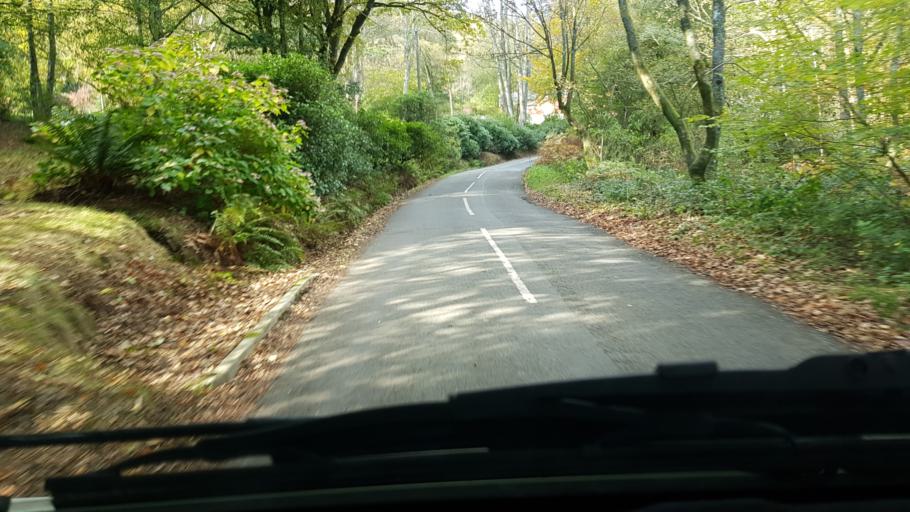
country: GB
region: England
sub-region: Surrey
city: Ockley
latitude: 51.1786
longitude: -0.3565
